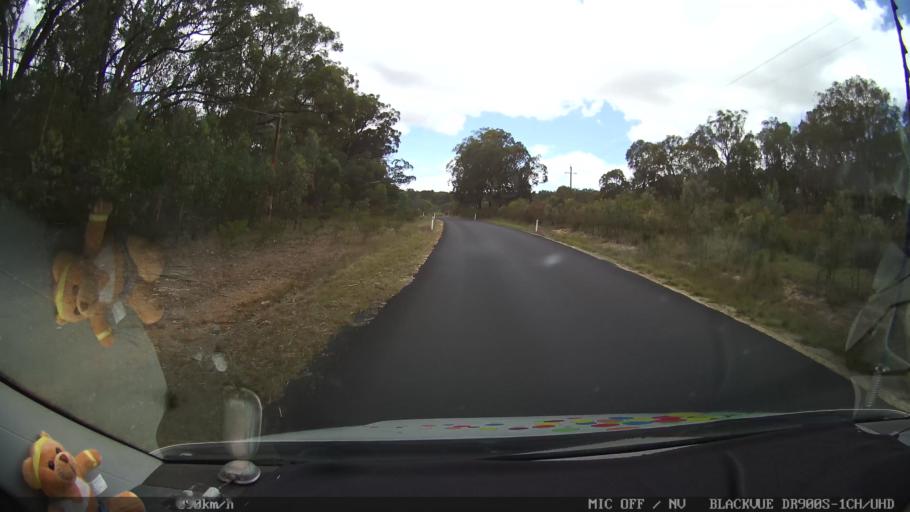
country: AU
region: New South Wales
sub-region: Glen Innes Severn
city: Glen Innes
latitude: -29.4384
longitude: 151.6271
